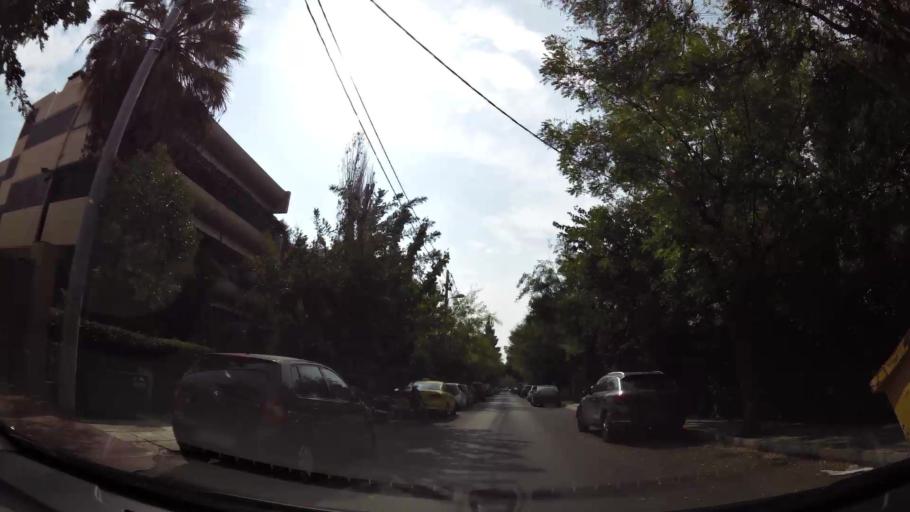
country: GR
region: Attica
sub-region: Nomarchia Athinas
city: Psychiko
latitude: 38.0103
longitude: 23.7781
